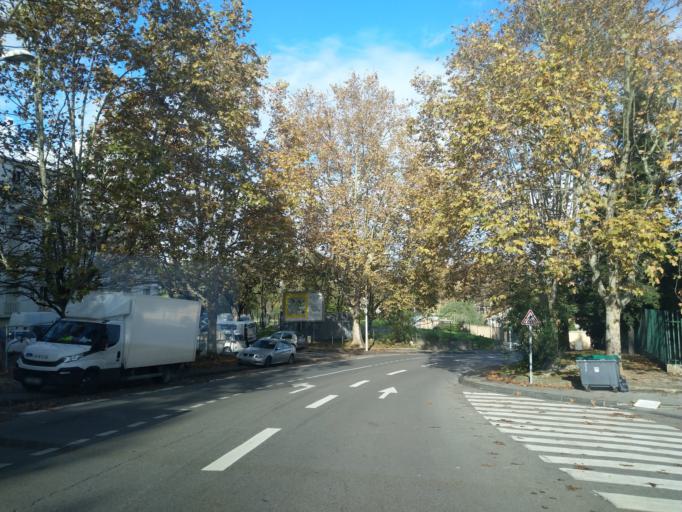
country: FR
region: Provence-Alpes-Cote d'Azur
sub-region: Departement des Bouches-du-Rhone
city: Marseille 12
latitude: 43.3197
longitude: 5.4388
